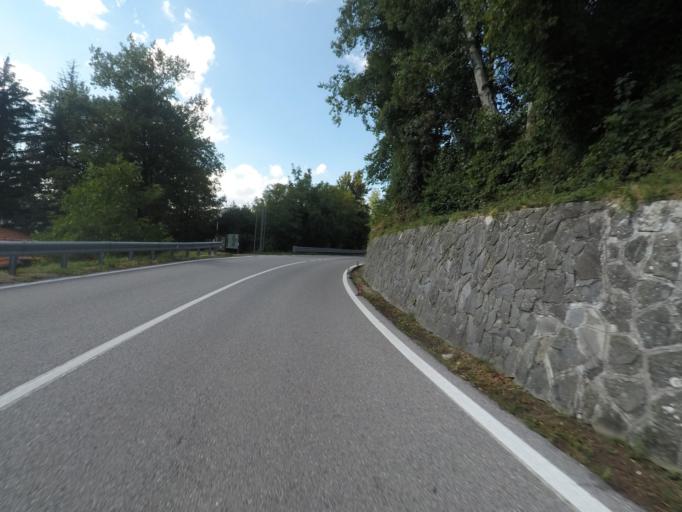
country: IT
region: Tuscany
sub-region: Provincia di Massa-Carrara
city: Comano
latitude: 44.2780
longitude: 10.1858
